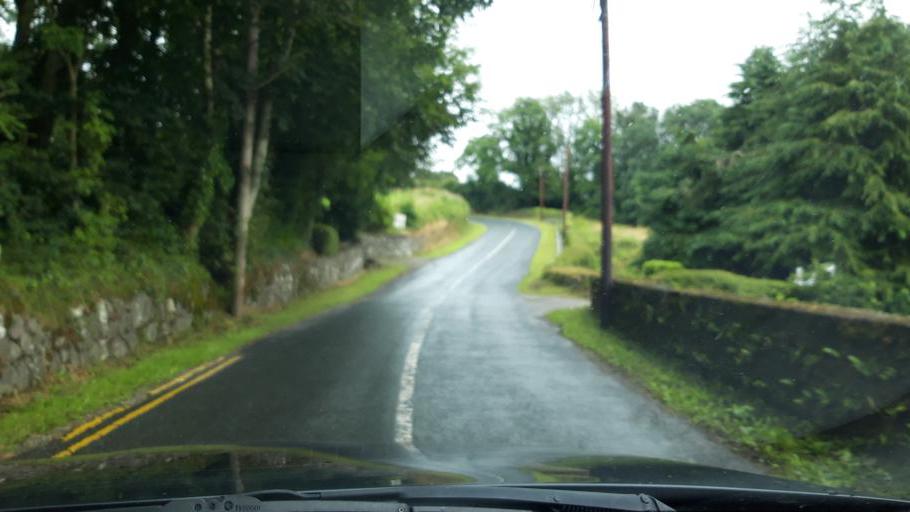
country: IE
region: Munster
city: Cahir
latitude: 52.1730
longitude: -7.8538
